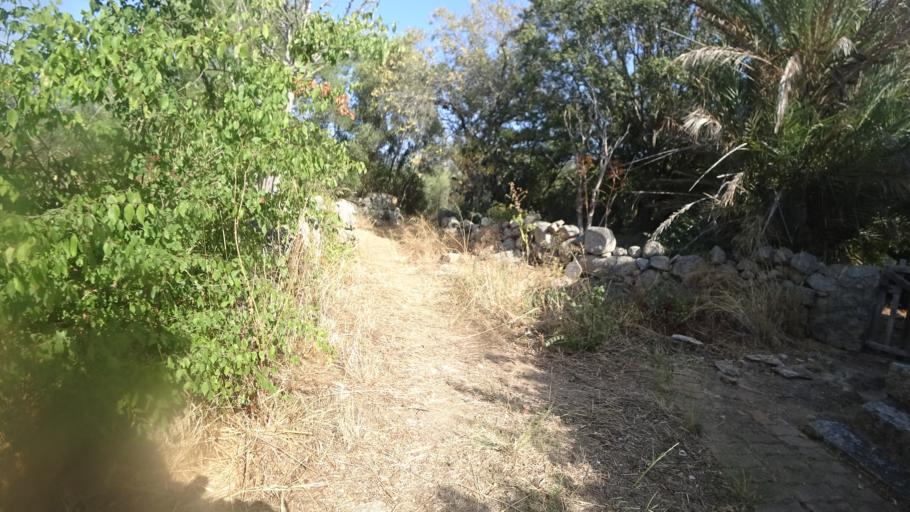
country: FR
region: Corsica
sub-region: Departement de la Corse-du-Sud
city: Porto-Vecchio
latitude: 41.6628
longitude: 9.3276
